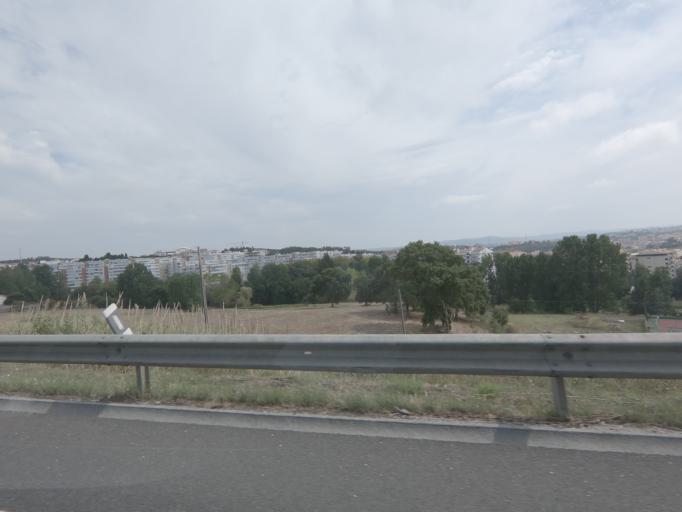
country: PT
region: Leiria
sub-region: Leiria
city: Leiria
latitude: 39.7596
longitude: -8.8074
